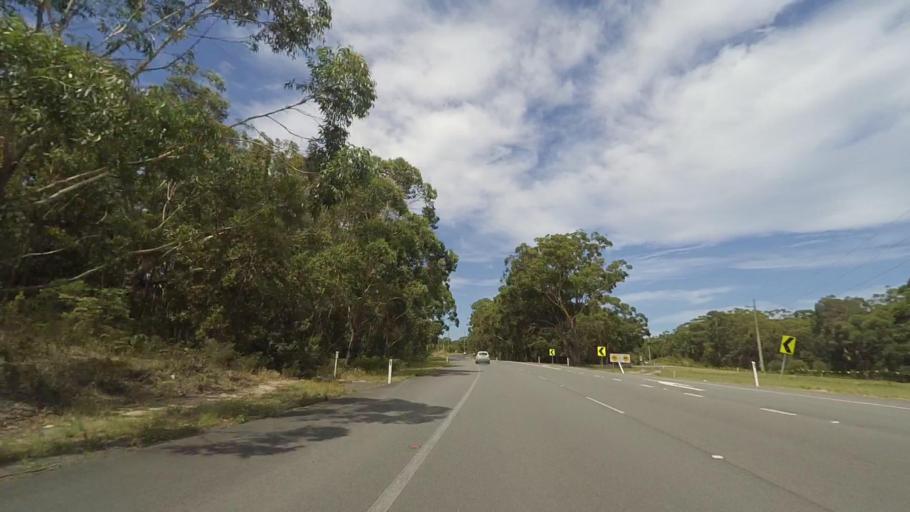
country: AU
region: New South Wales
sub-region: Port Stephens Shire
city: Medowie
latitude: -32.7857
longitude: 151.9702
